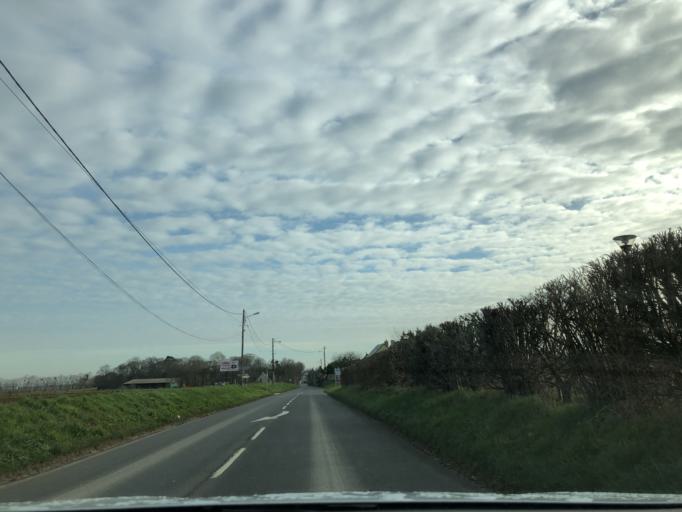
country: FR
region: Lower Normandy
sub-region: Departement du Calvados
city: Cresserons
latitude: 49.2922
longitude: -0.3597
